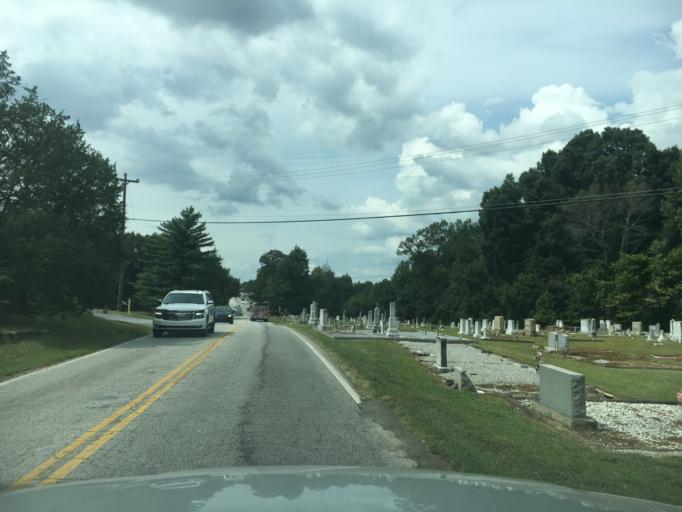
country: US
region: South Carolina
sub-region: Greenville County
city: Five Forks
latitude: 34.8481
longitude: -82.2261
